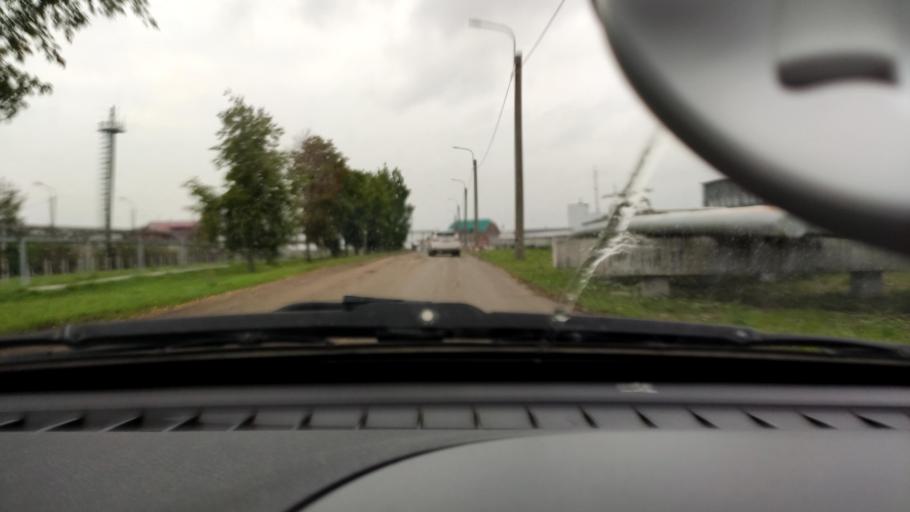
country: RU
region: Perm
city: Gamovo
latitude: 57.9098
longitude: 56.1472
